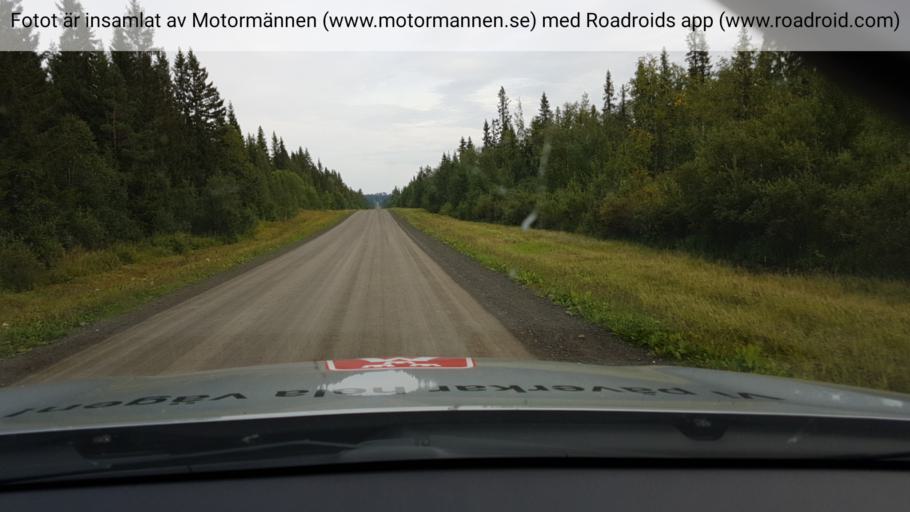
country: SE
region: Jaemtland
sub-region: OEstersunds Kommun
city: Lit
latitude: 63.6641
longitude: 14.9039
